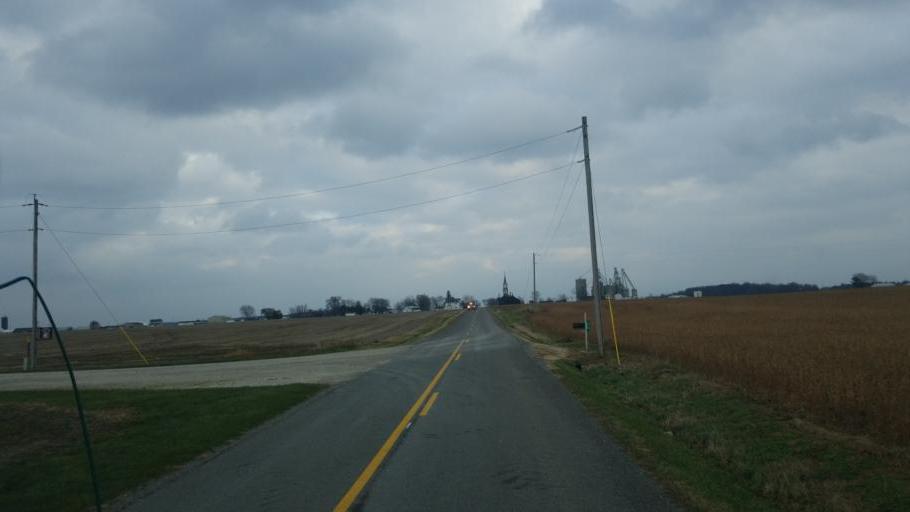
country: US
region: Ohio
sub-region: Mercer County
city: Fort Recovery
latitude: 40.5091
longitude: -84.7929
